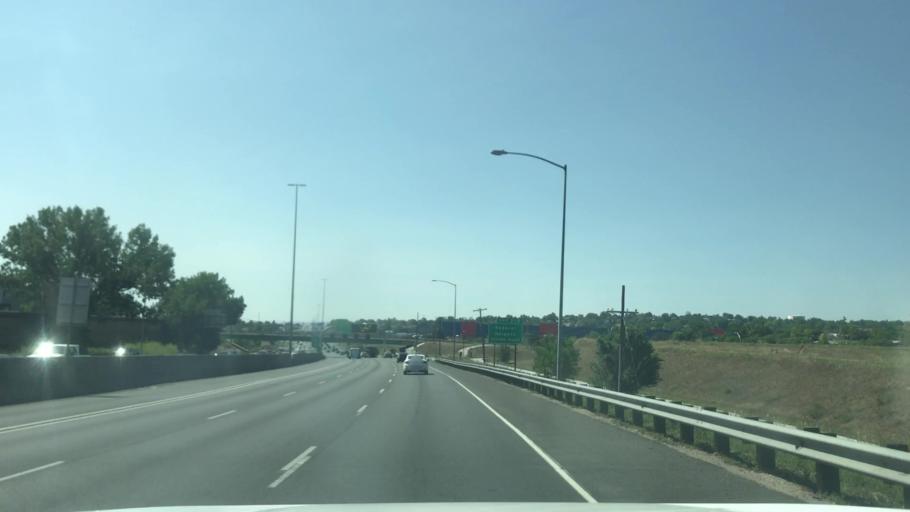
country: US
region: Colorado
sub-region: Adams County
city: Federal Heights
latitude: 39.8592
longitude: -104.9877
